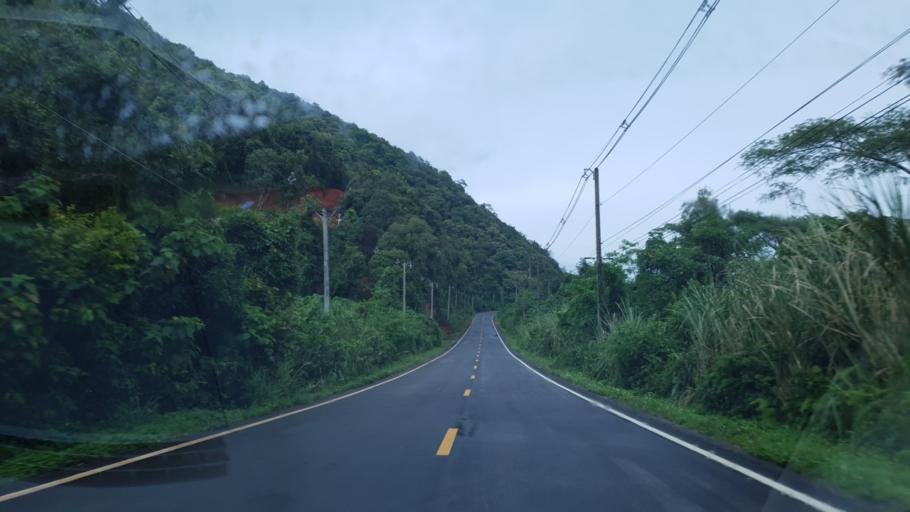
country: TH
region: Mae Hong Son
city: Ban Huai I Huak
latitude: 18.1464
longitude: 98.1007
